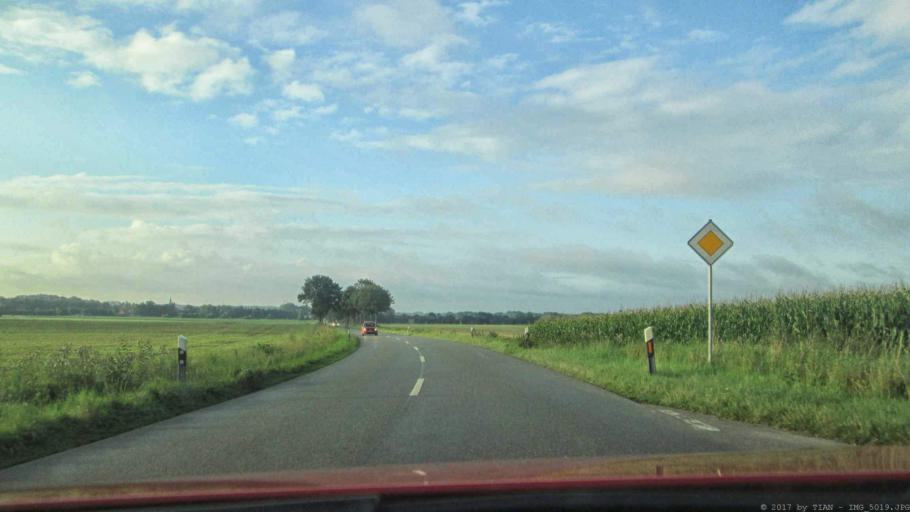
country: DE
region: Lower Saxony
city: Emmendorf
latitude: 53.0154
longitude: 10.5987
